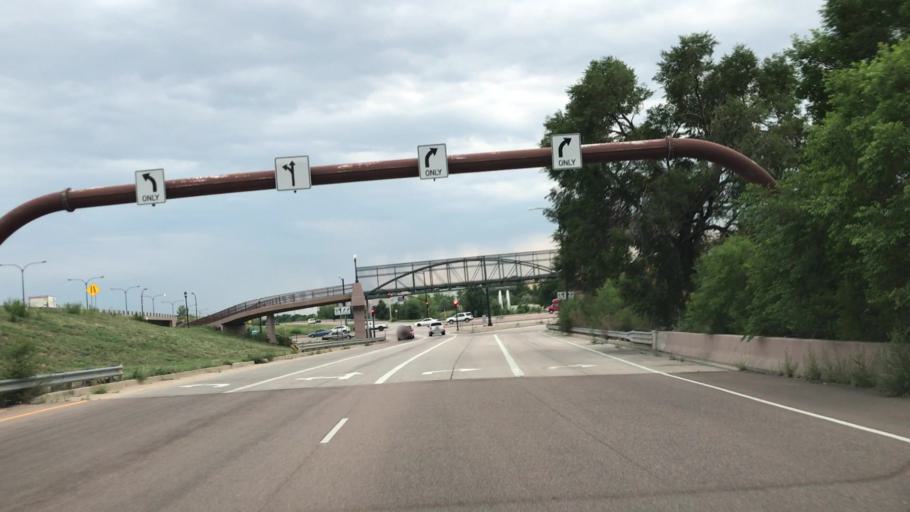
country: US
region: Colorado
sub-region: El Paso County
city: Stratmoor
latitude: 38.7972
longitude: -104.7985
